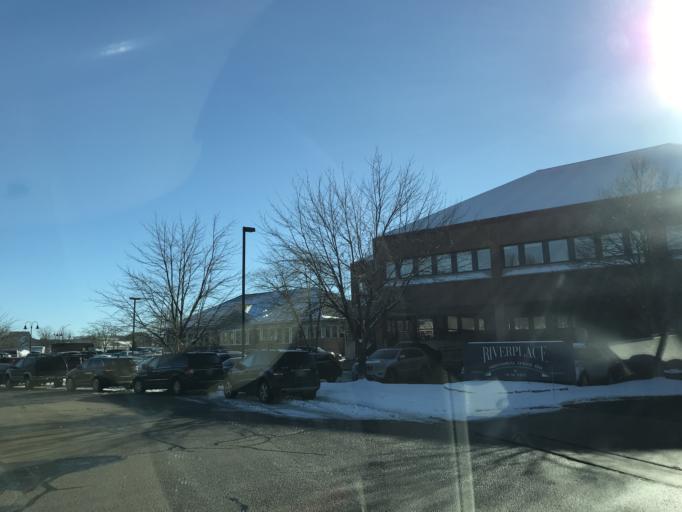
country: US
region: Wisconsin
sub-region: Dane County
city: Monona
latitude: 43.0470
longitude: -89.3269
